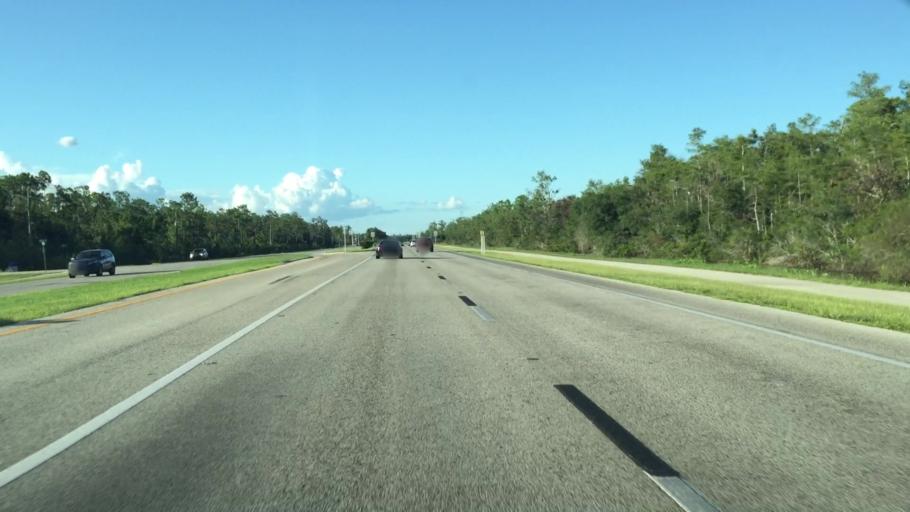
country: US
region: Florida
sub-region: Lee County
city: Villas
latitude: 26.5642
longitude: -81.8308
